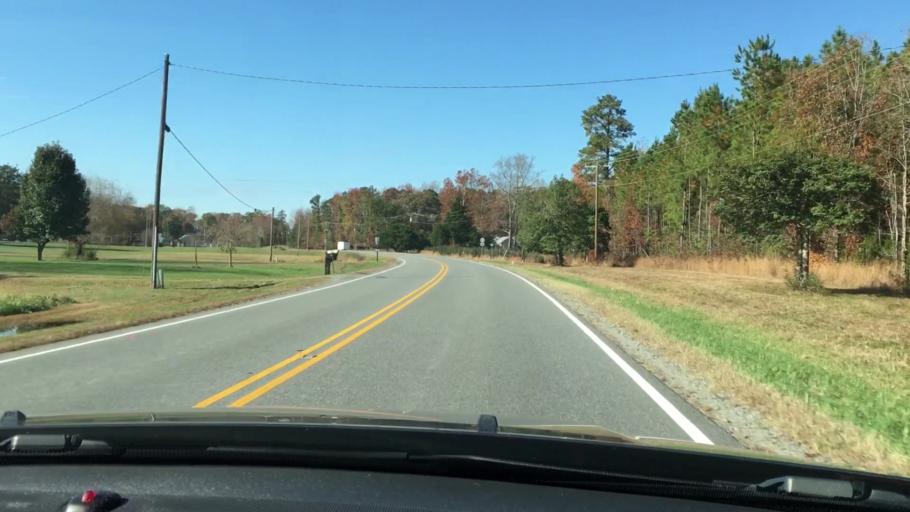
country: US
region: Virginia
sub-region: King William County
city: King William
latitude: 37.6716
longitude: -76.9731
